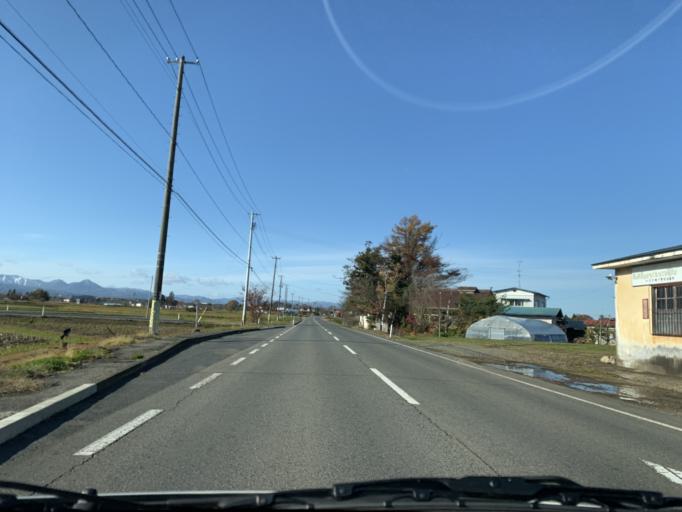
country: JP
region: Iwate
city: Mizusawa
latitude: 39.1788
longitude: 141.1346
